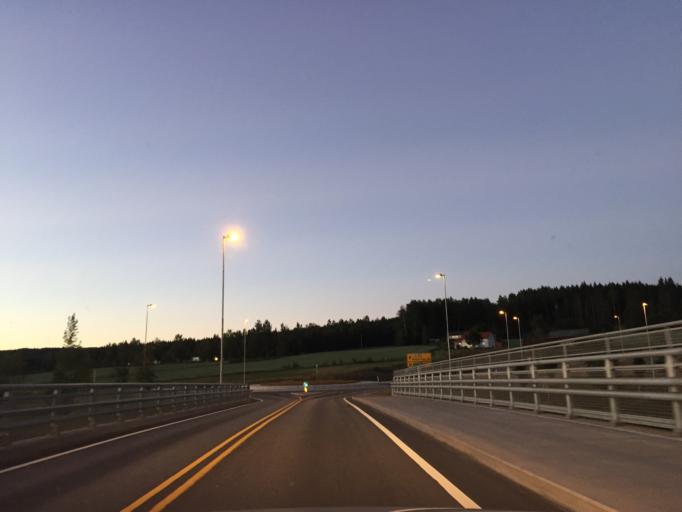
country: NO
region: Hedmark
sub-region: Kongsvinger
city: Spetalen
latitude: 60.2082
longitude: 11.8898
